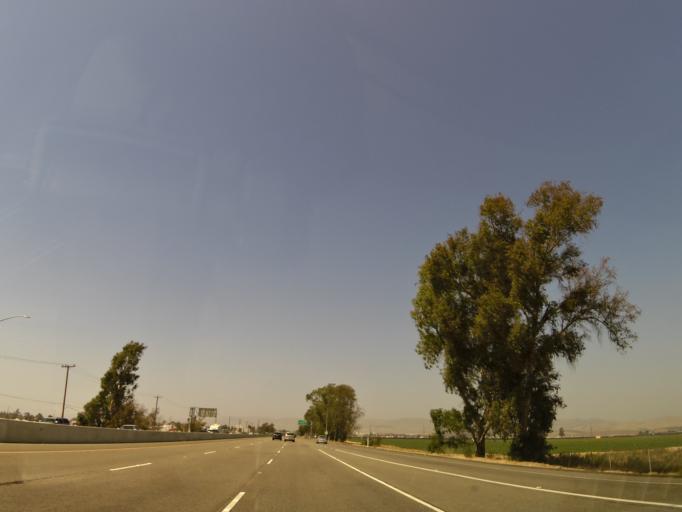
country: US
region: California
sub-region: Santa Barbara County
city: Santa Maria
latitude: 34.9257
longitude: -120.4178
